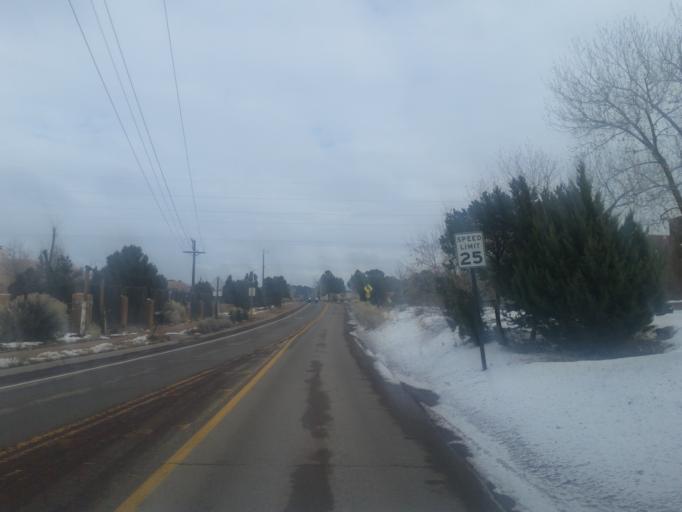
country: US
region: New Mexico
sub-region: Santa Fe County
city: Santa Fe
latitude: 35.6861
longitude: -105.9165
